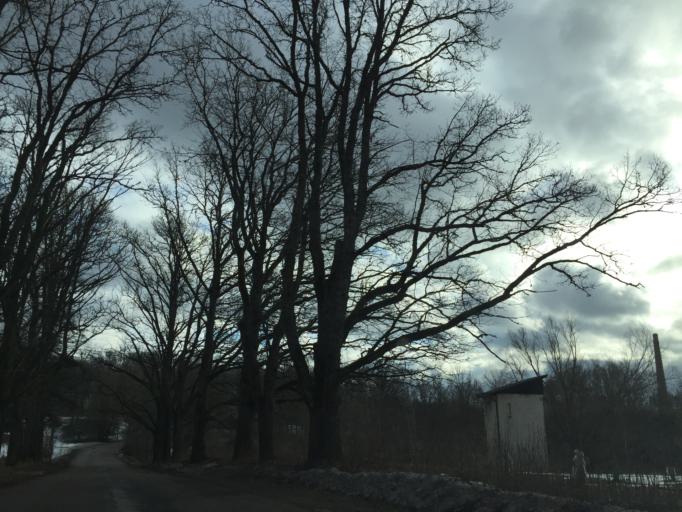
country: LV
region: Aloja
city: Aloja
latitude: 57.7755
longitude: 24.8119
